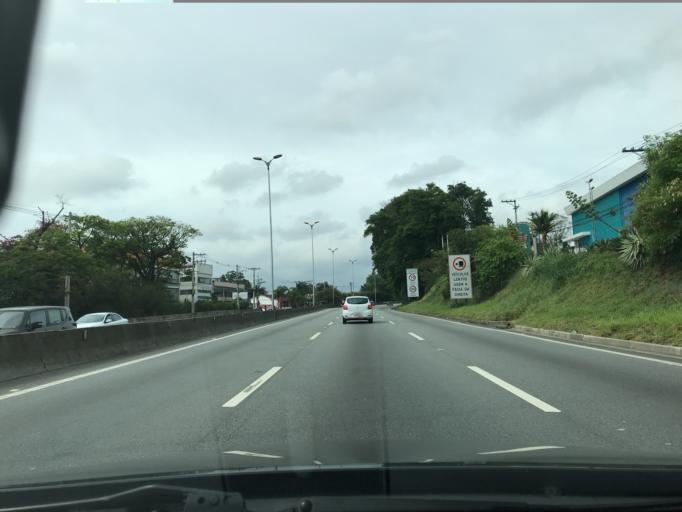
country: BR
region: Sao Paulo
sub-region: Embu
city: Embu
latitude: -23.5952
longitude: -46.8398
